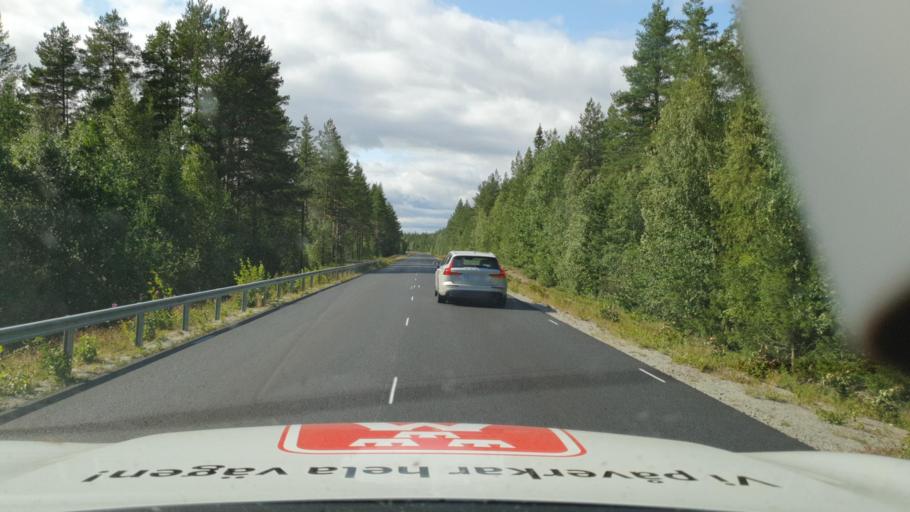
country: SE
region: Vaesterbotten
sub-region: Asele Kommun
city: Asele
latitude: 64.1981
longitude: 17.0672
